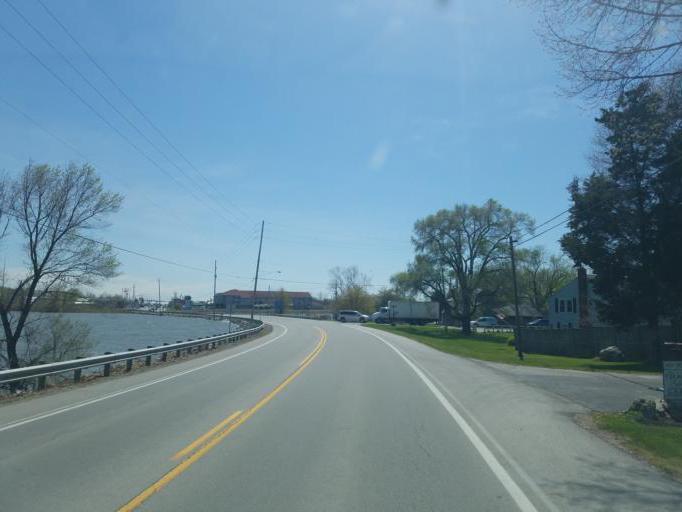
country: US
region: Ohio
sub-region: Ottawa County
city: Port Clinton
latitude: 41.5287
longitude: -82.8586
